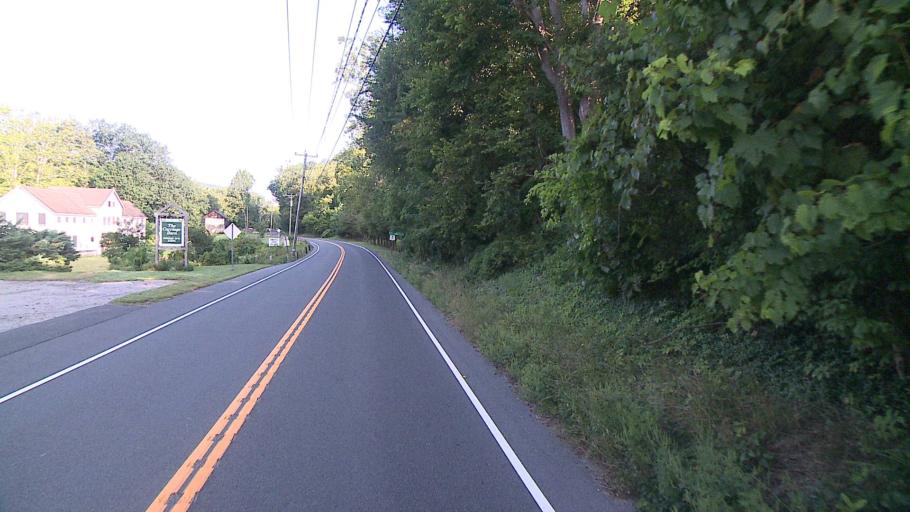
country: US
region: Connecticut
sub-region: Fairfield County
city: Sherman
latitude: 41.6491
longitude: -73.4846
